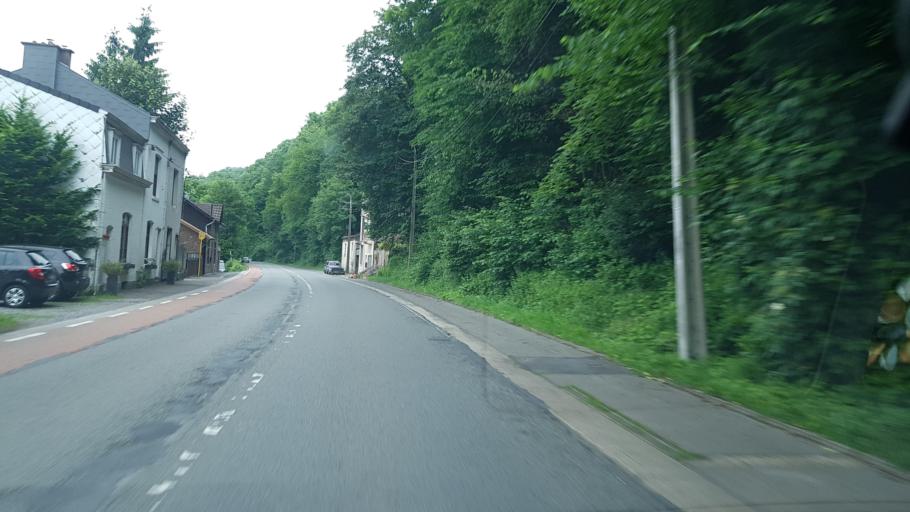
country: BE
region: Wallonia
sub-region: Province de Liege
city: Limbourg
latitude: 50.6026
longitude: 5.9015
